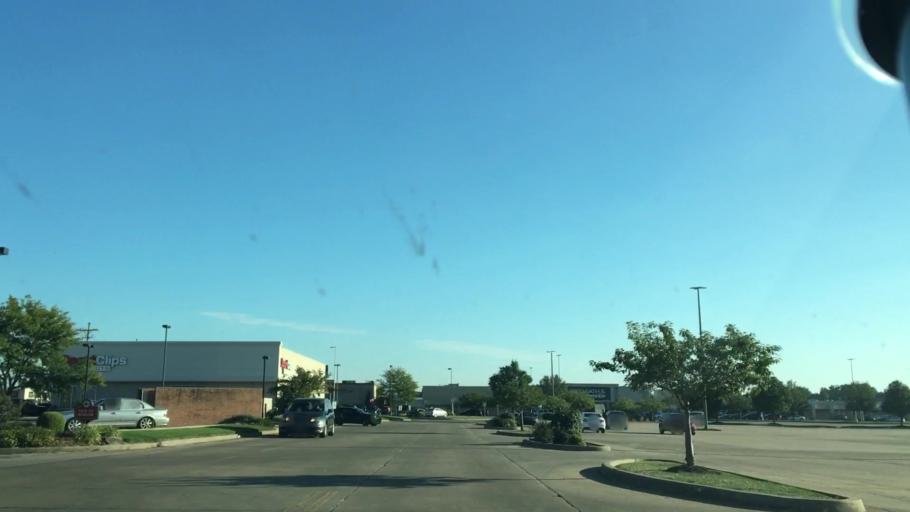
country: US
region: Indiana
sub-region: Vanderburgh County
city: Melody Hill
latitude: 37.9826
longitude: -87.4936
